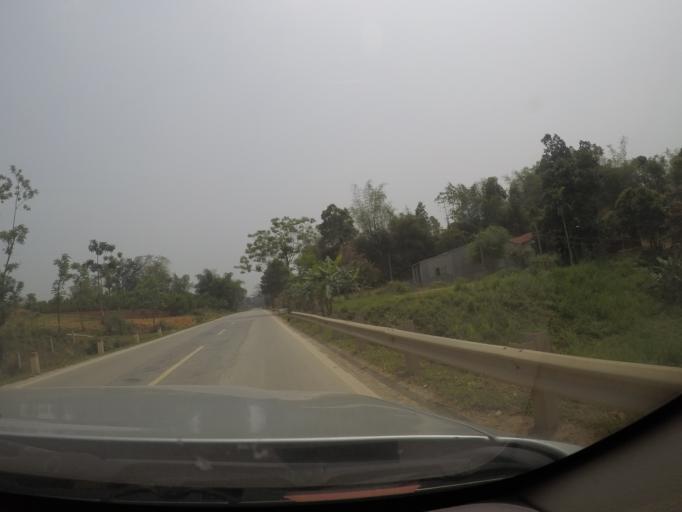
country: VN
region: Thanh Hoa
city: Thi Tran Yen Cat
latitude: 19.7094
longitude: 105.4391
